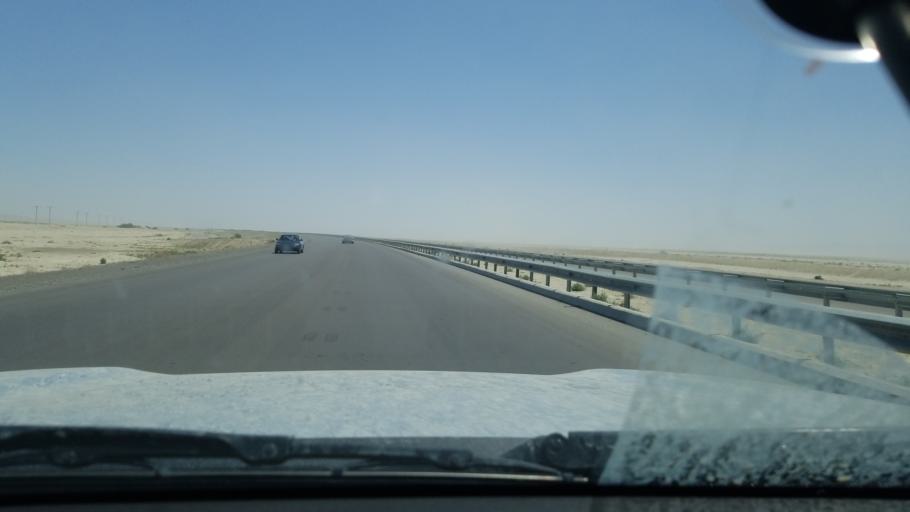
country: TM
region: Balkan
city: Gazanjyk
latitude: 39.2258
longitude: 55.0636
